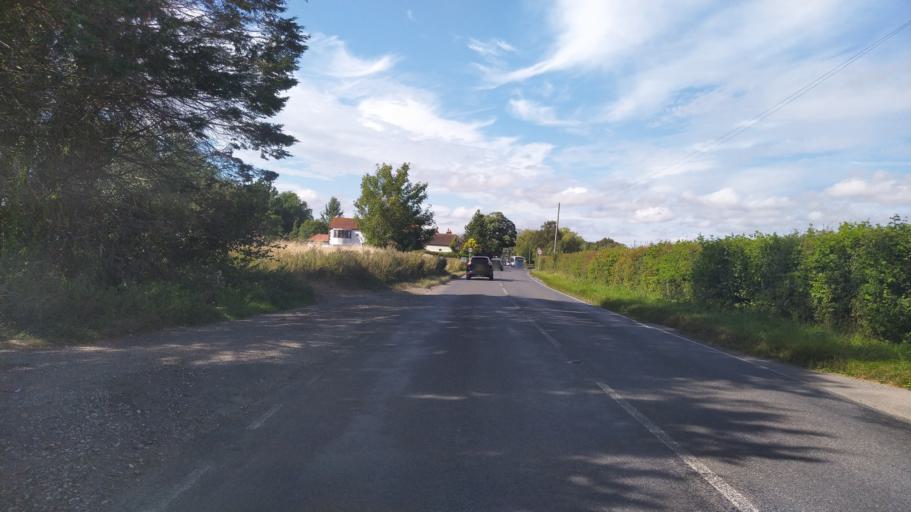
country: GB
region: England
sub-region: West Sussex
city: Chichester
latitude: 50.8178
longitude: -0.7685
